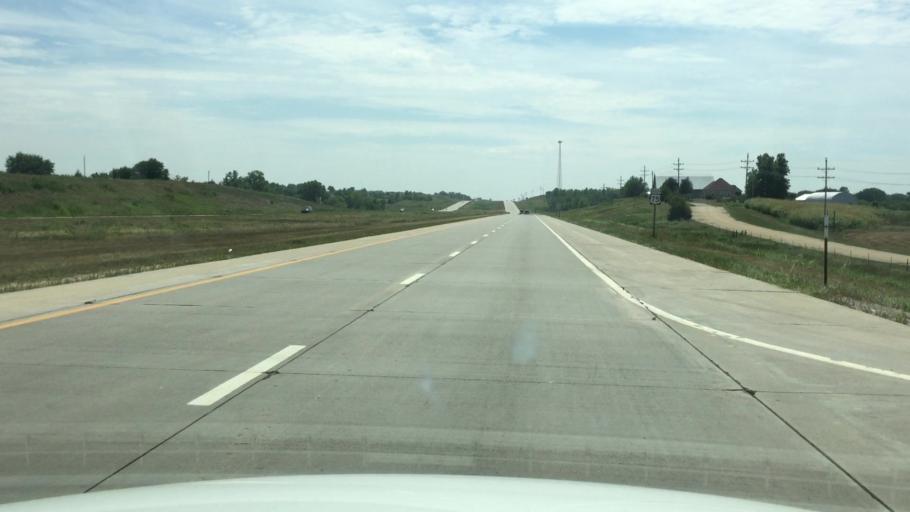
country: US
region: Kansas
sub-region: Jackson County
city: Holton
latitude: 39.2597
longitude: -95.7201
